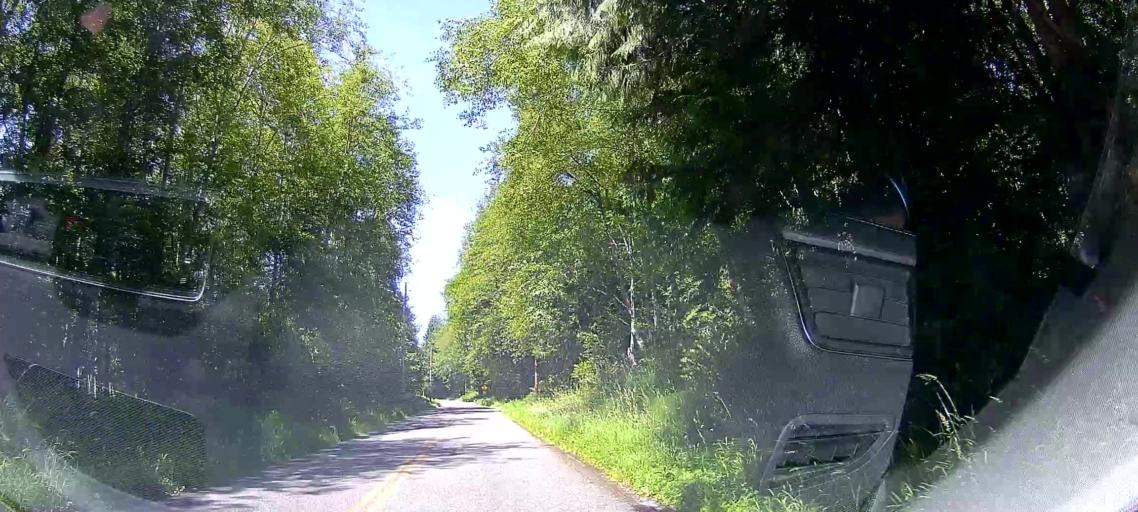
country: US
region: Washington
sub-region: Whatcom County
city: Sudden Valley
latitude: 48.6099
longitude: -122.3179
